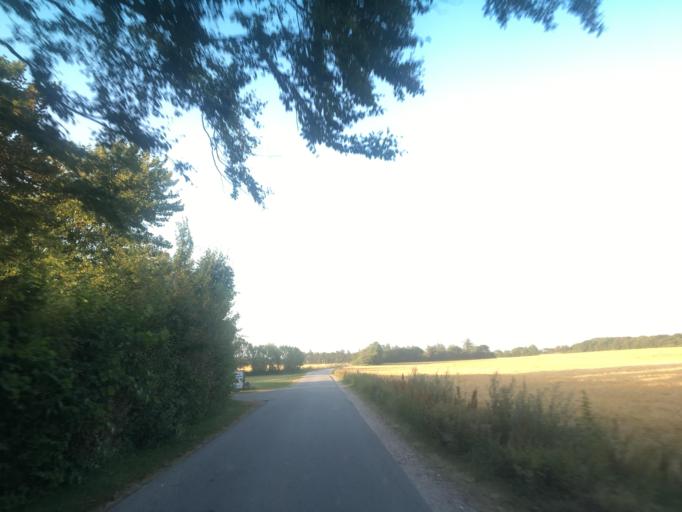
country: DK
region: North Denmark
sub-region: Thisted Kommune
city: Hurup
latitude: 56.8326
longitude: 8.3466
